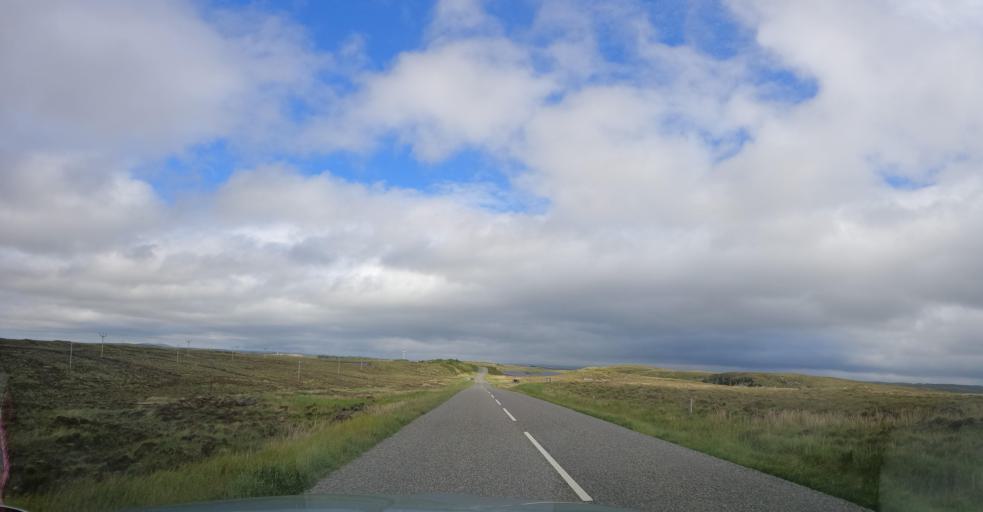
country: GB
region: Scotland
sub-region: Eilean Siar
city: Stornoway
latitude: 58.1860
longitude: -6.4523
